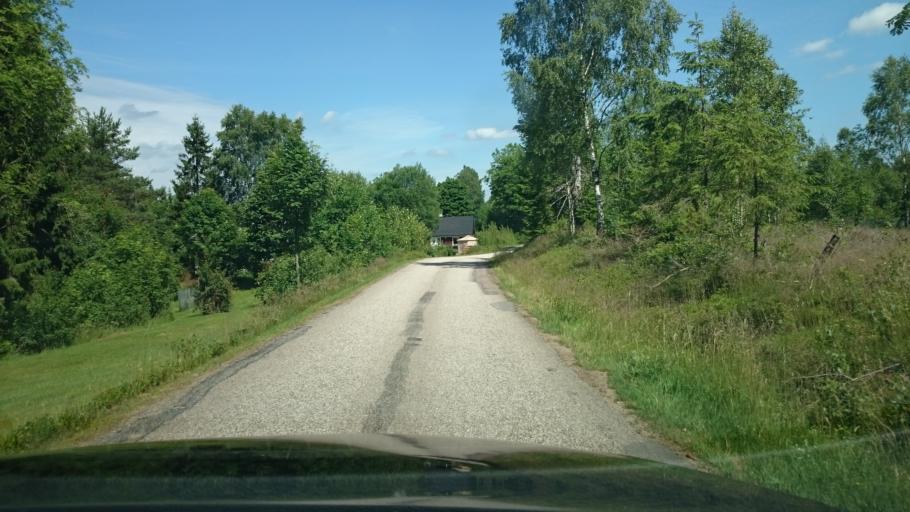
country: SE
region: Halland
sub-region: Hylte Kommun
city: Hyltebruk
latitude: 56.9752
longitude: 13.2042
